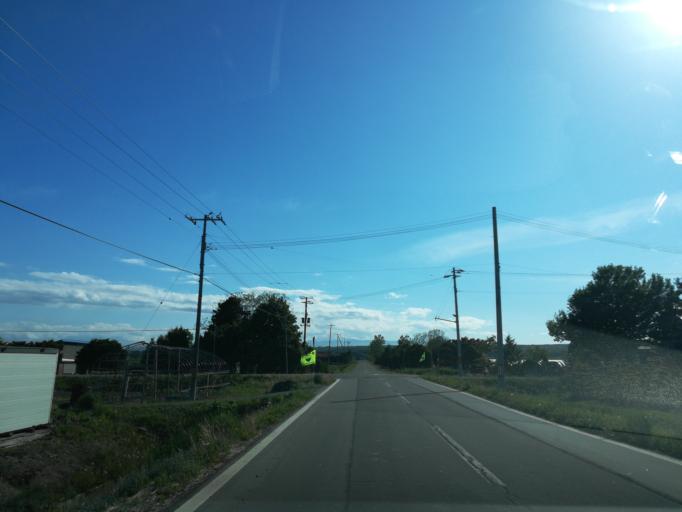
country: JP
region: Hokkaido
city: Kitahiroshima
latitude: 43.0350
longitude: 141.5734
